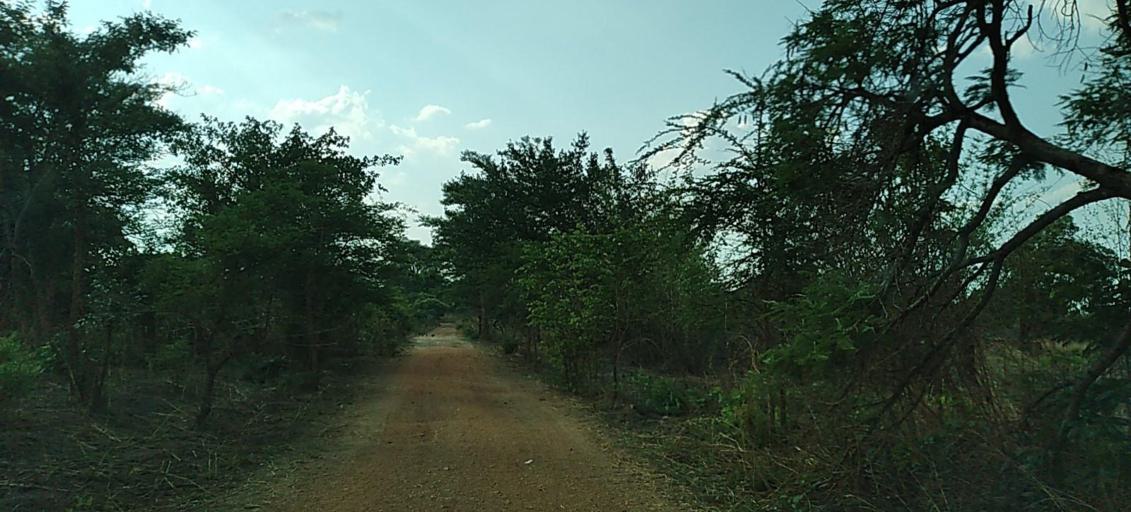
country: ZM
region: Copperbelt
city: Mpongwe
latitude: -13.4742
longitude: 28.0744
